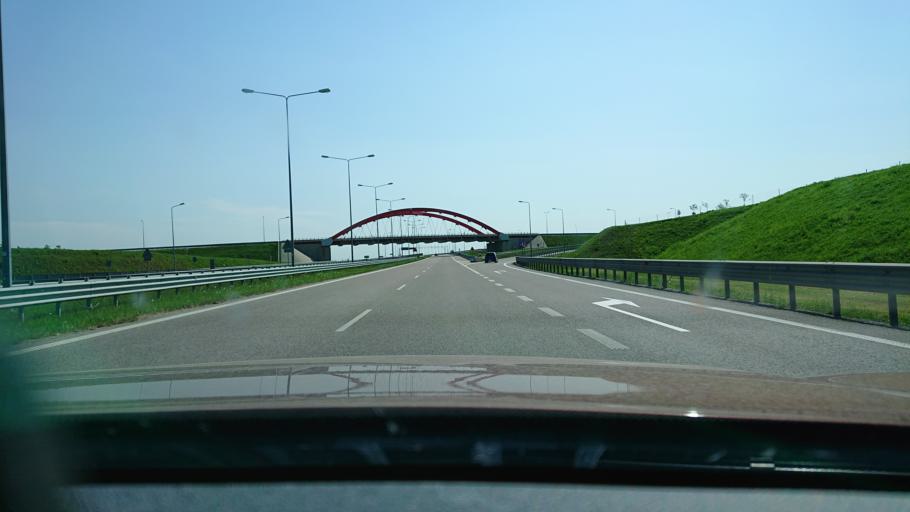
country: PL
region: Subcarpathian Voivodeship
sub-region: Powiat jaroslawski
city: Radymno
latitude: 49.9119
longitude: 22.8066
